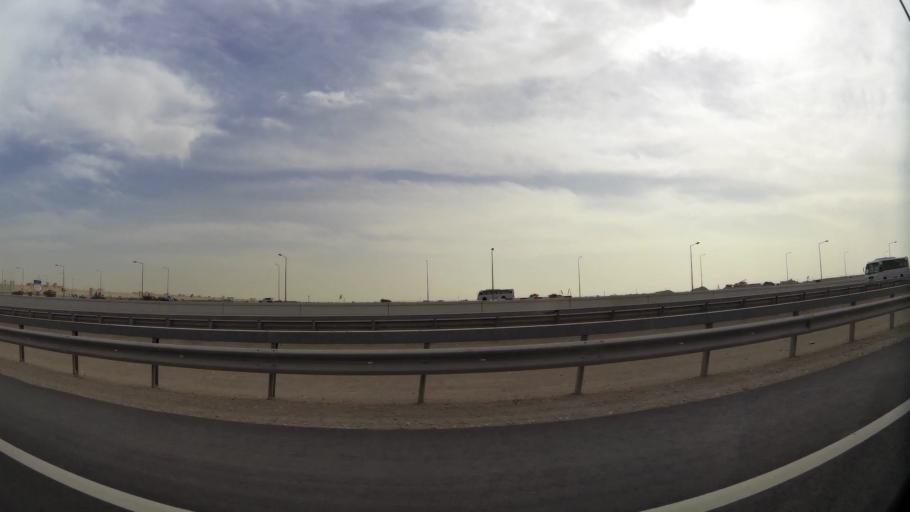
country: QA
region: Baladiyat ar Rayyan
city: Ar Rayyan
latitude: 25.3234
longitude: 51.3474
